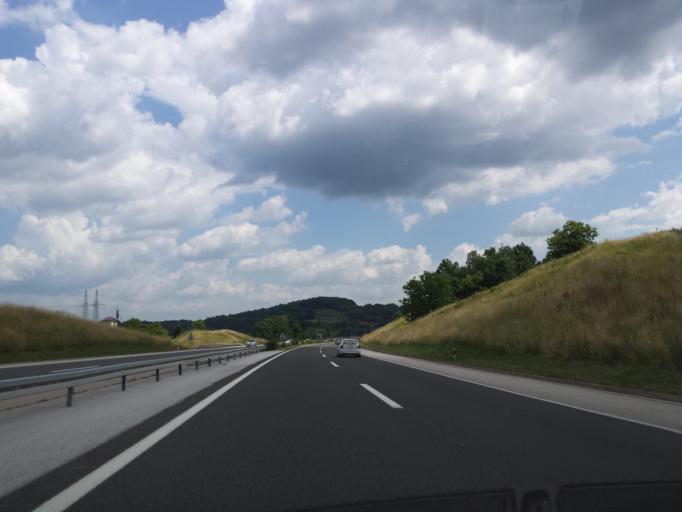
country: HR
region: Karlovacka
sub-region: Grad Karlovac
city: Karlovac
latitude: 45.5112
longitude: 15.4685
